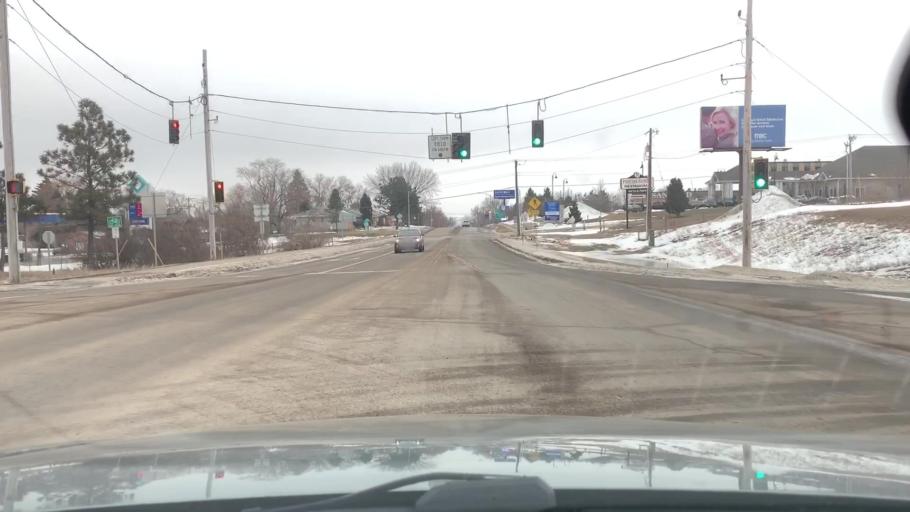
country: US
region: North Dakota
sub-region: Morton County
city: Mandan
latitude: 46.8439
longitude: -100.9070
